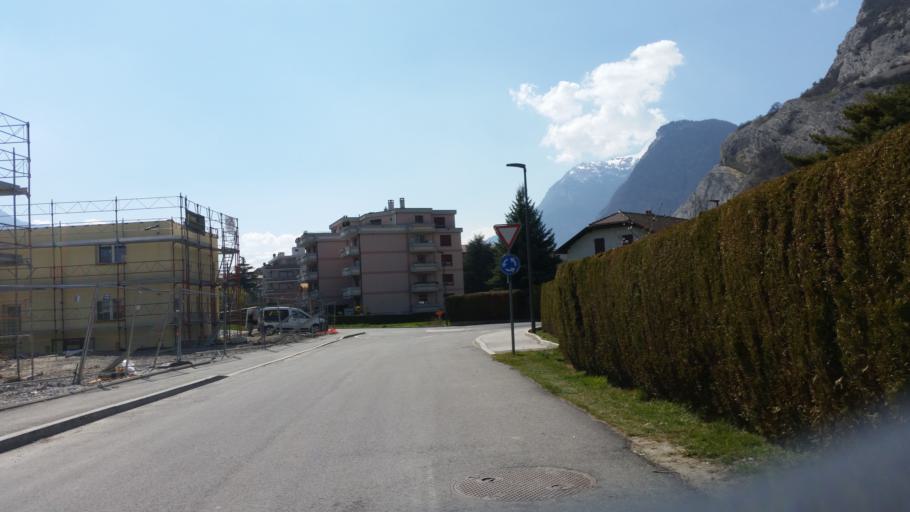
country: CH
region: Valais
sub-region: Conthey District
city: Ardon
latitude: 46.2076
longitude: 7.2563
